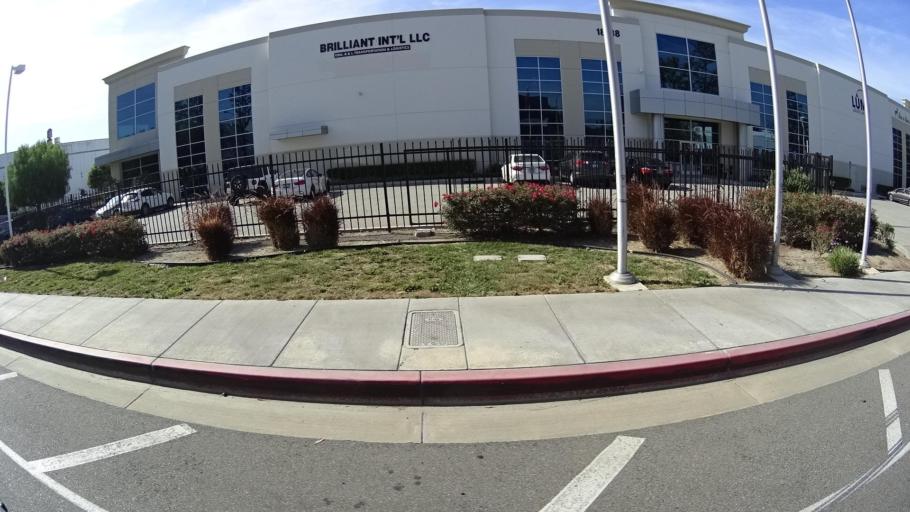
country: US
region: California
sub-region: Los Angeles County
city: South San Jose Hills
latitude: 33.9994
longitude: -117.8953
